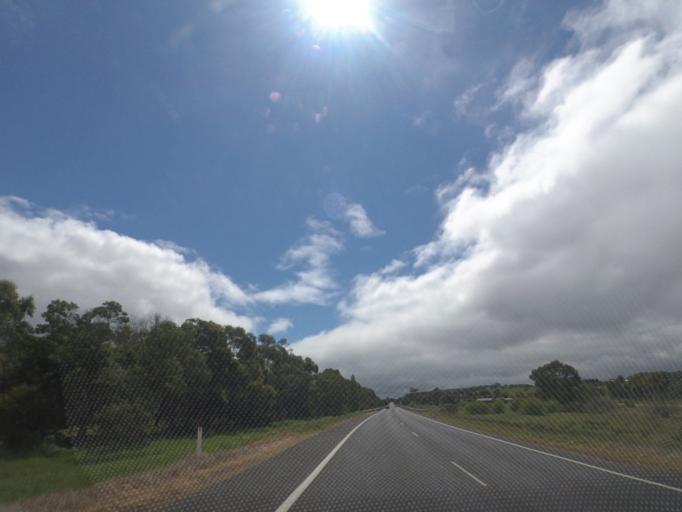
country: AU
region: Victoria
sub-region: Ballarat North
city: Lake Wendouree
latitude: -37.4775
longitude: 143.8463
